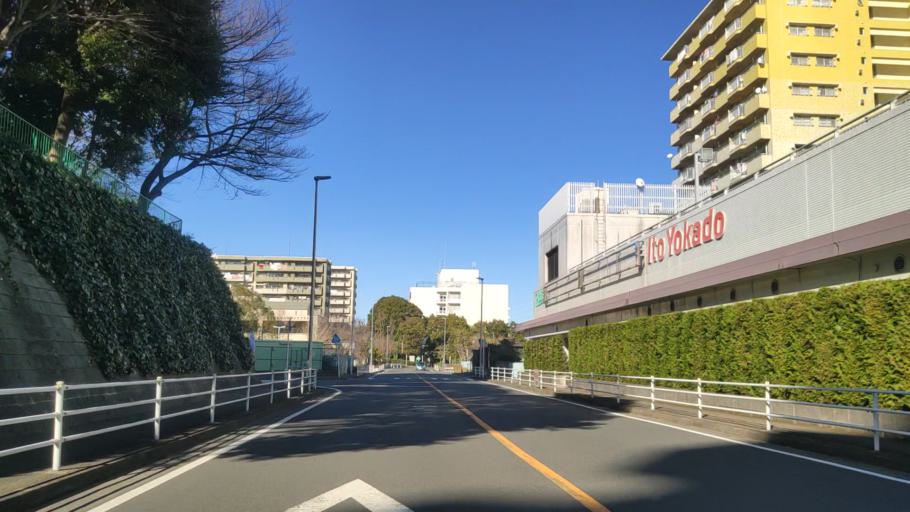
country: JP
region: Kanagawa
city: Minami-rinkan
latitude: 35.5051
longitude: 139.4974
